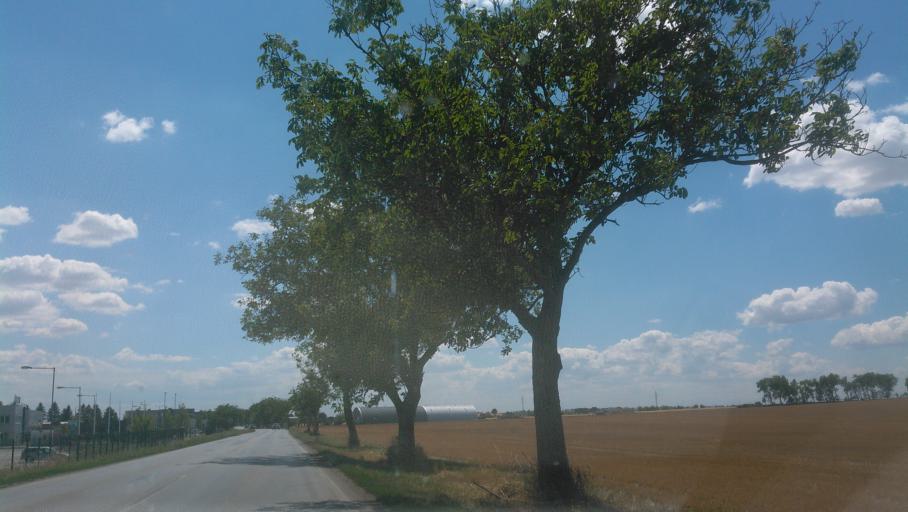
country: SK
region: Trnavsky
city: Vrbove
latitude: 48.6053
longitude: 17.7499
